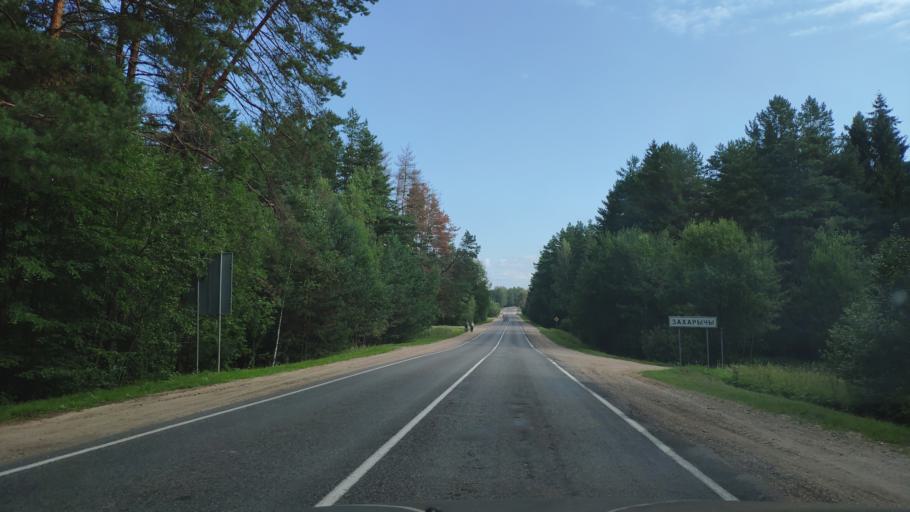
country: BY
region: Minsk
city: Zaslawye
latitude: 53.9811
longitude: 27.2534
